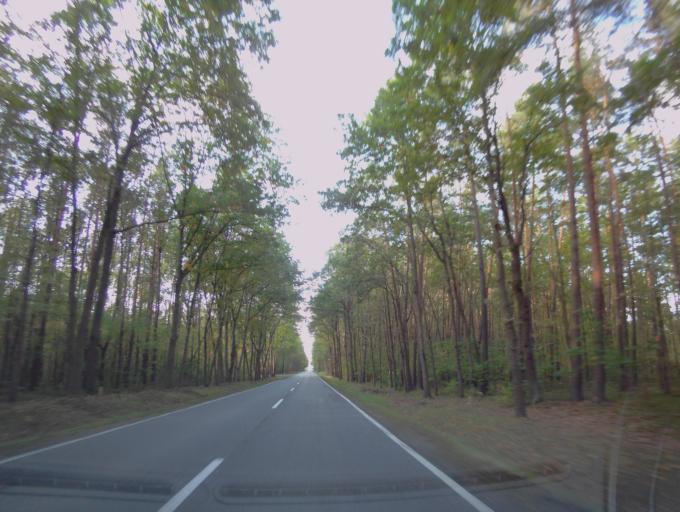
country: PL
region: Subcarpathian Voivodeship
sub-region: Powiat nizanski
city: Krzeszow
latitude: 50.3926
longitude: 22.3017
